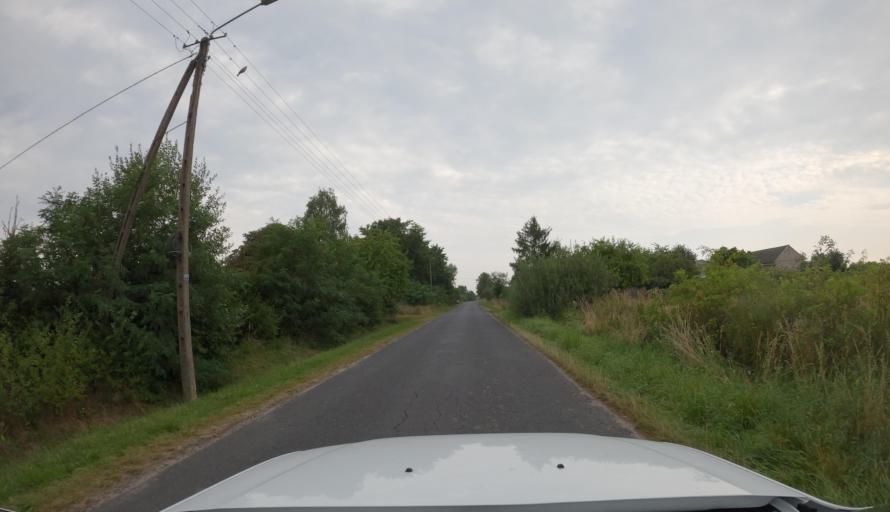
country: PL
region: West Pomeranian Voivodeship
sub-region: Powiat swidwinski
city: Slawoborze
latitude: 53.7917
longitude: 15.6012
